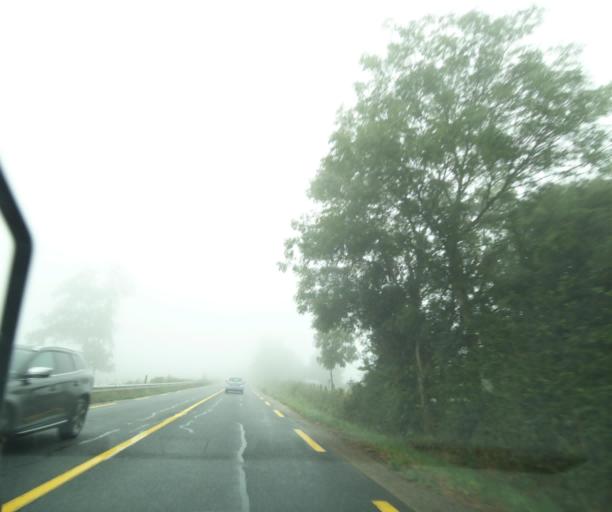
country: FR
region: Midi-Pyrenees
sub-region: Departement de l'Aveyron
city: Baraqueville
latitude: 44.2532
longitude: 2.4130
